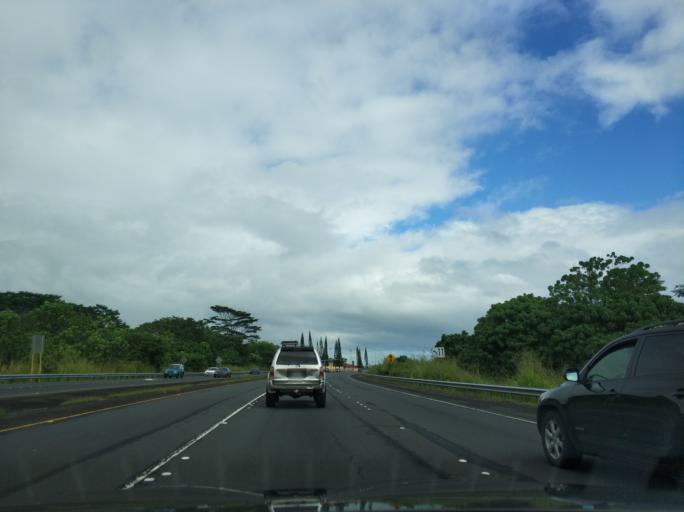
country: US
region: Hawaii
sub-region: Hawaii County
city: Kea'au
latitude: 19.6083
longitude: -155.0290
